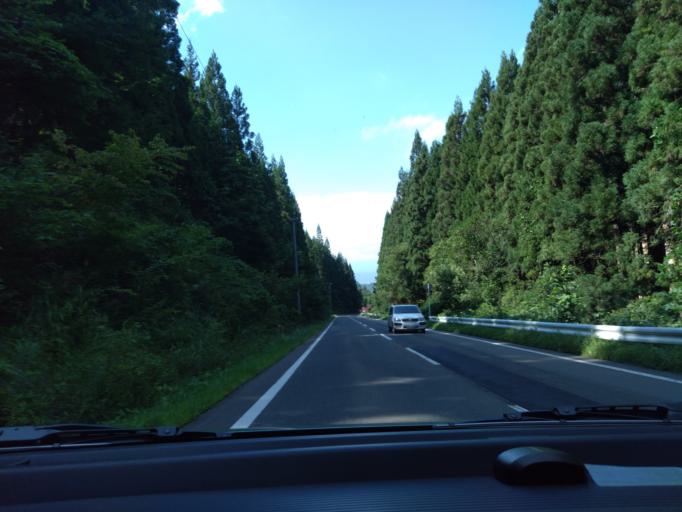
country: JP
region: Iwate
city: Shizukuishi
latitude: 39.6389
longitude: 141.0067
